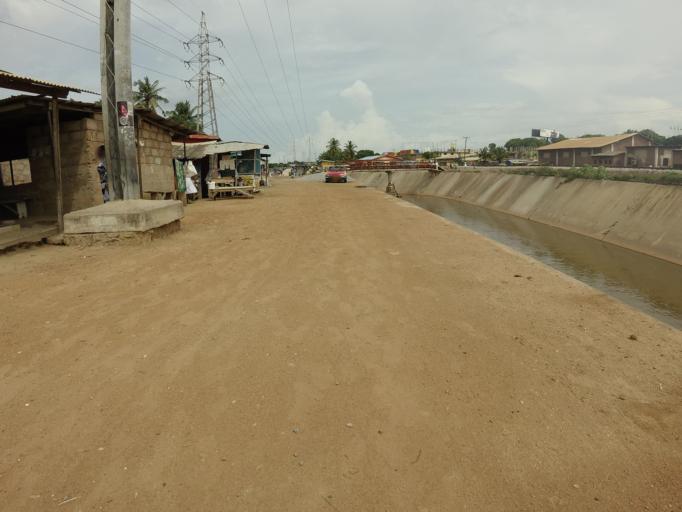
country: GH
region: Greater Accra
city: Accra
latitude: 5.5955
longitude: -0.2200
